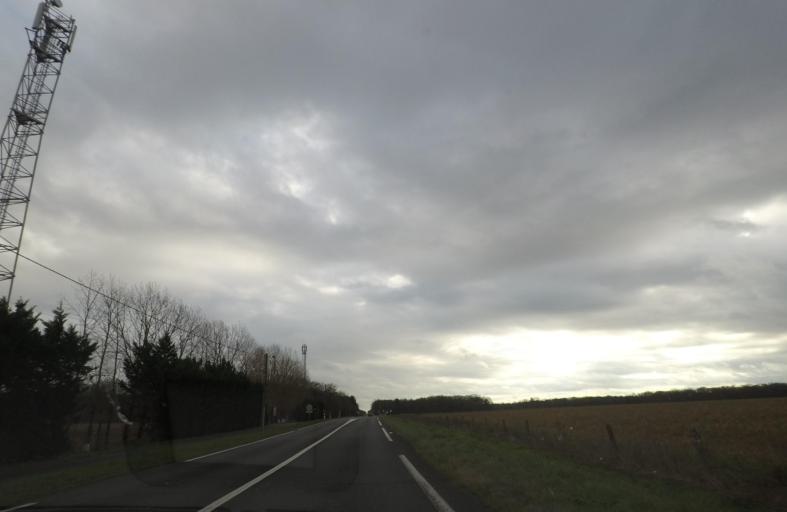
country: FR
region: Centre
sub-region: Departement du Loir-et-Cher
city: Soings-en-Sologne
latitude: 47.4322
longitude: 1.5625
